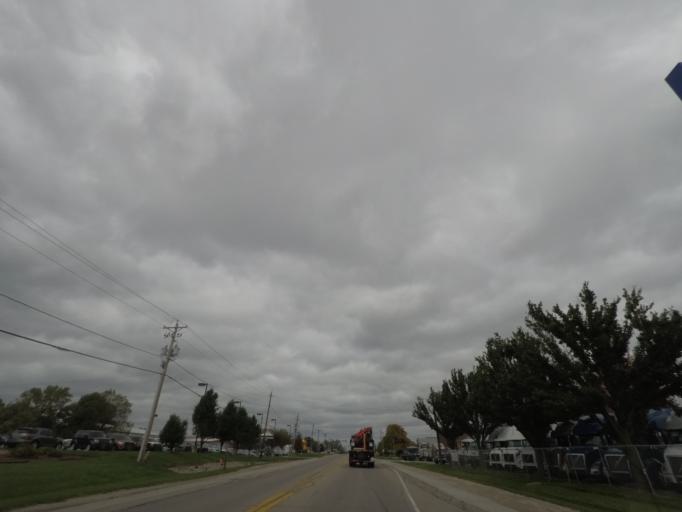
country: US
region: Iowa
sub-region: Polk County
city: Saylorville
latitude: 41.6565
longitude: -93.6005
